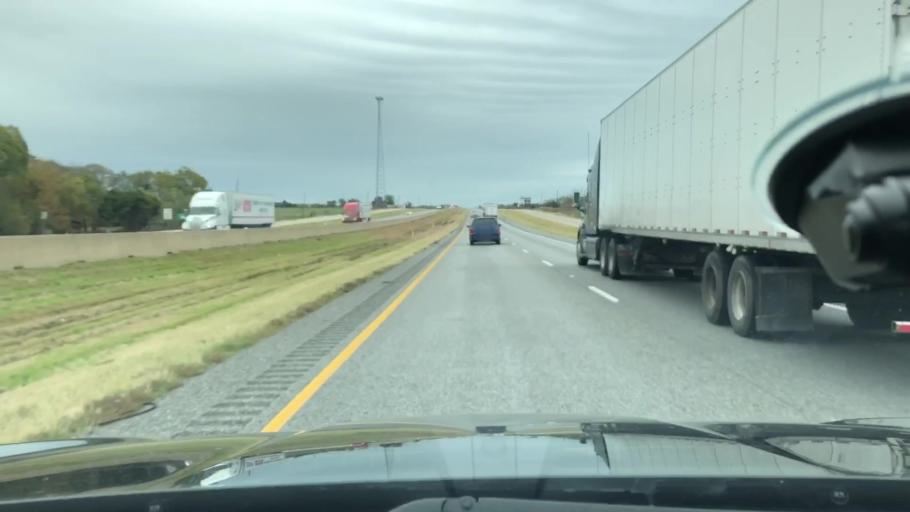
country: US
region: Texas
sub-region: Hunt County
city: Commerce
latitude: 33.1299
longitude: -95.8814
